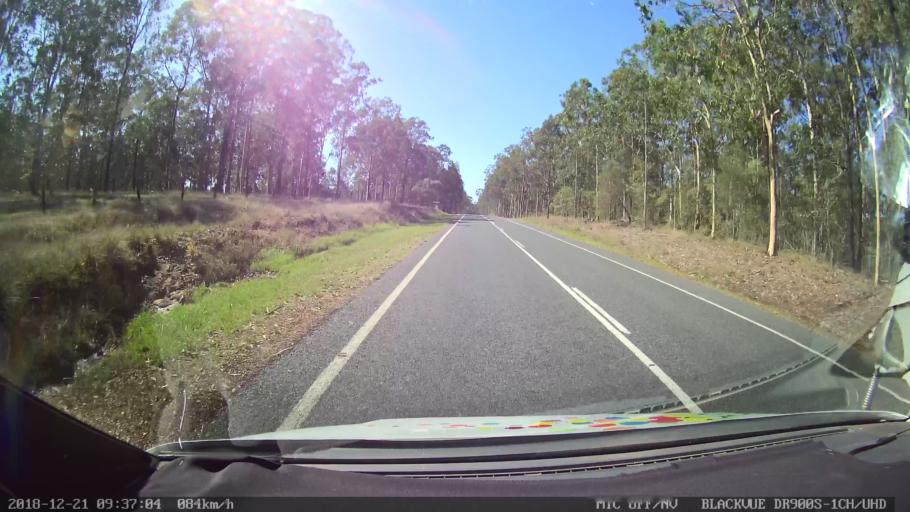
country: AU
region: New South Wales
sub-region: Clarence Valley
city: Grafton
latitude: -29.5317
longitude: 152.9854
